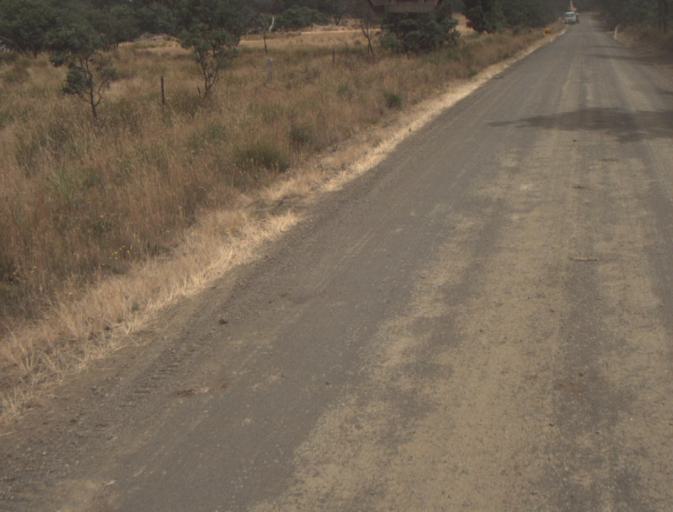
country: AU
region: Tasmania
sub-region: Northern Midlands
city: Evandale
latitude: -41.5180
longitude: 147.3558
